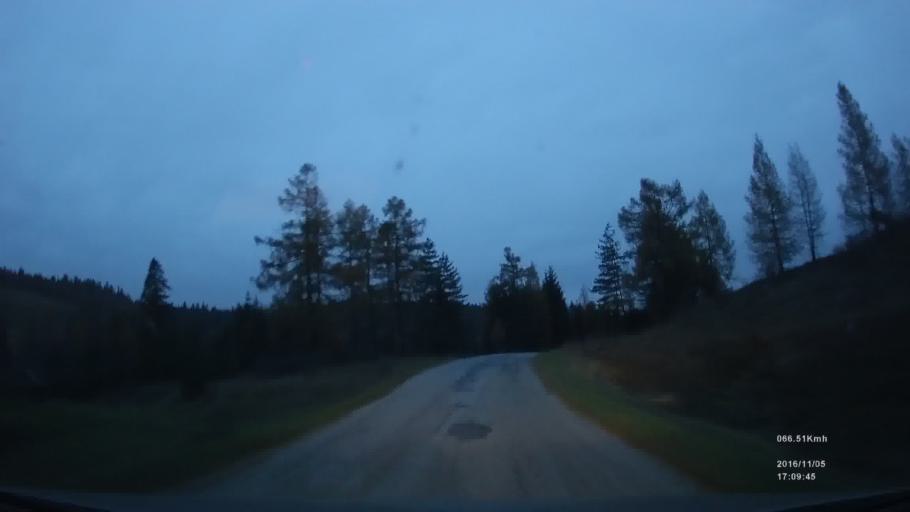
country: SK
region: Presovsky
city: Lubica
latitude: 49.0571
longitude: 20.5123
